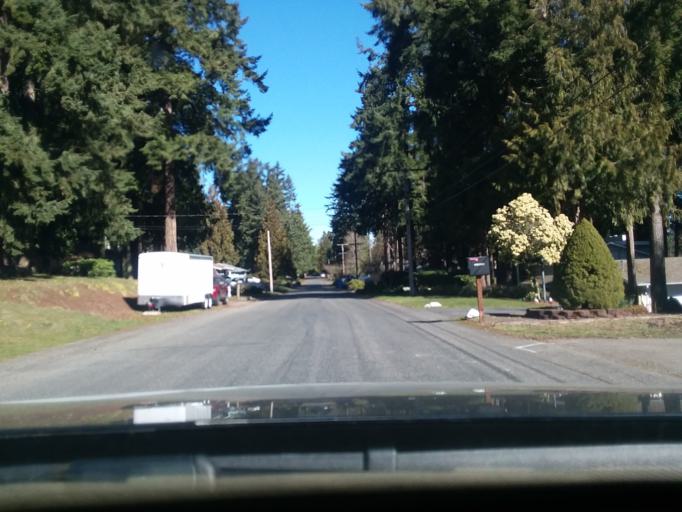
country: US
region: Washington
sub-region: Pierce County
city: Summit
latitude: 47.1634
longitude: -122.3435
